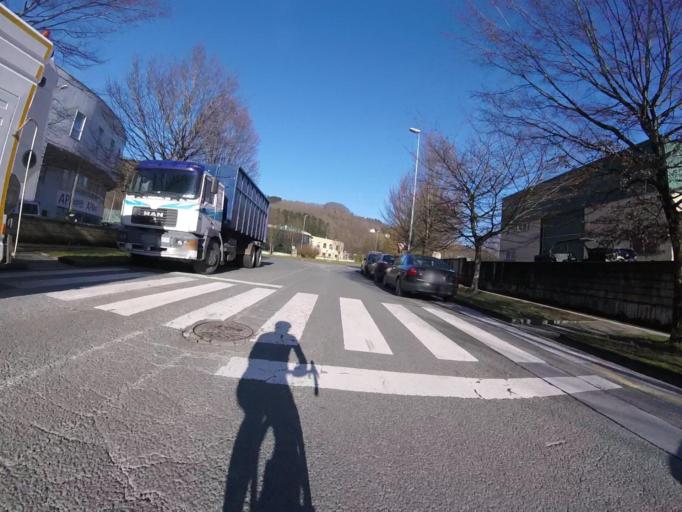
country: ES
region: Navarre
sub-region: Provincia de Navarra
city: Bera
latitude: 43.2796
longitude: -1.6958
